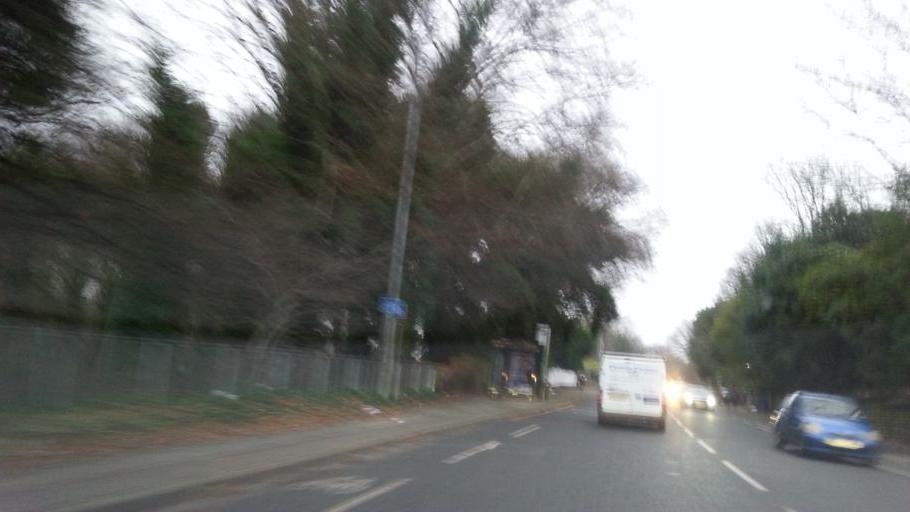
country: GB
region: England
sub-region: Manchester
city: Crumpsall
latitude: 53.5095
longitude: -2.2627
